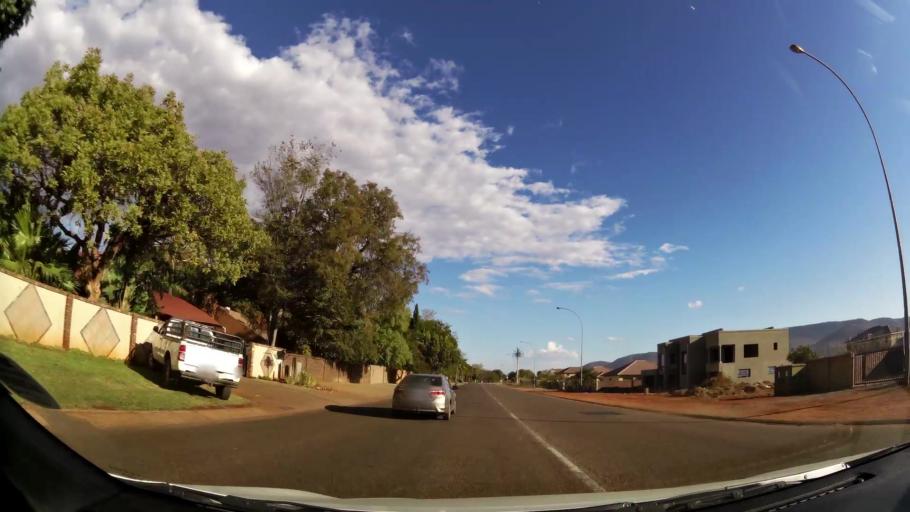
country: ZA
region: Limpopo
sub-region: Waterberg District Municipality
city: Mokopane
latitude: -24.2011
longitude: 29.0020
